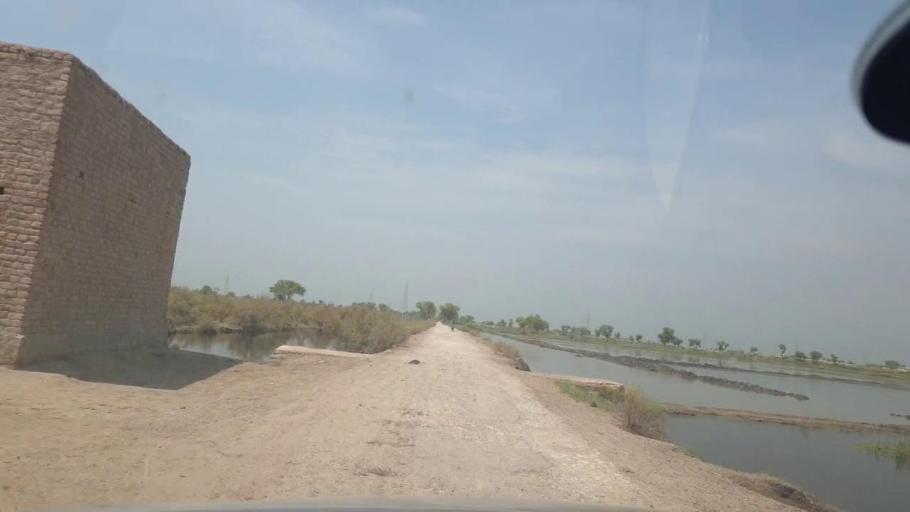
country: PK
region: Sindh
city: Thul
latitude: 28.1771
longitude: 68.6222
